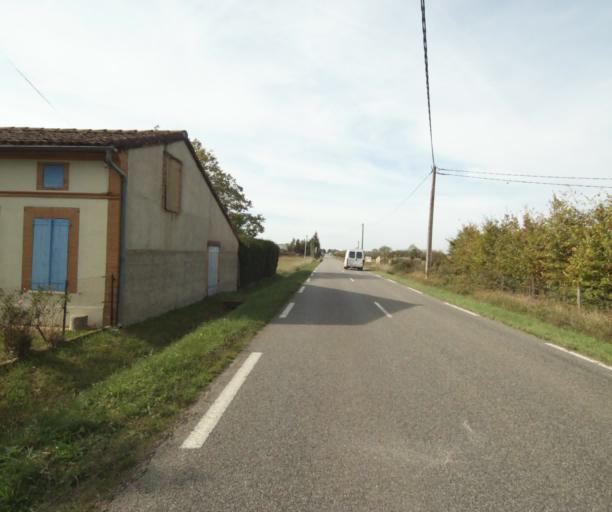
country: FR
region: Midi-Pyrenees
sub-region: Departement du Tarn-et-Garonne
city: Labastide-Saint-Pierre
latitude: 43.9118
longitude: 1.3857
